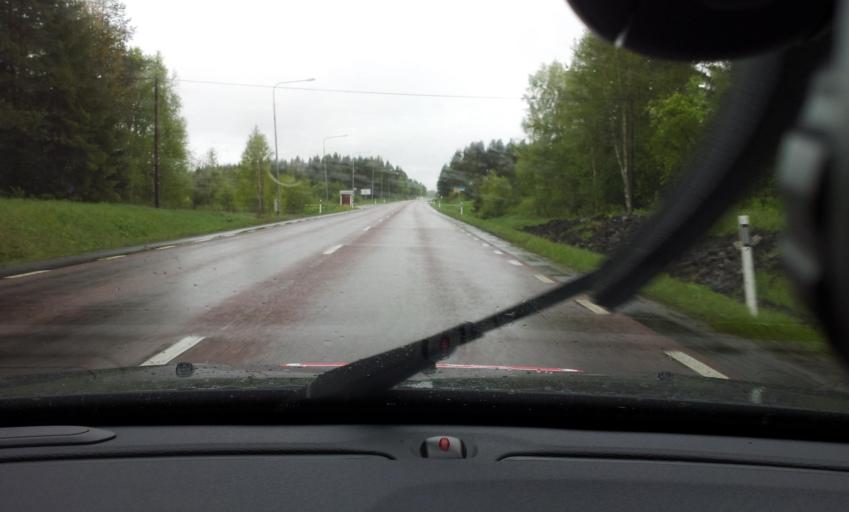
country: SE
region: Jaemtland
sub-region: Bergs Kommun
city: Hoverberg
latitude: 62.9278
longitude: 14.5364
